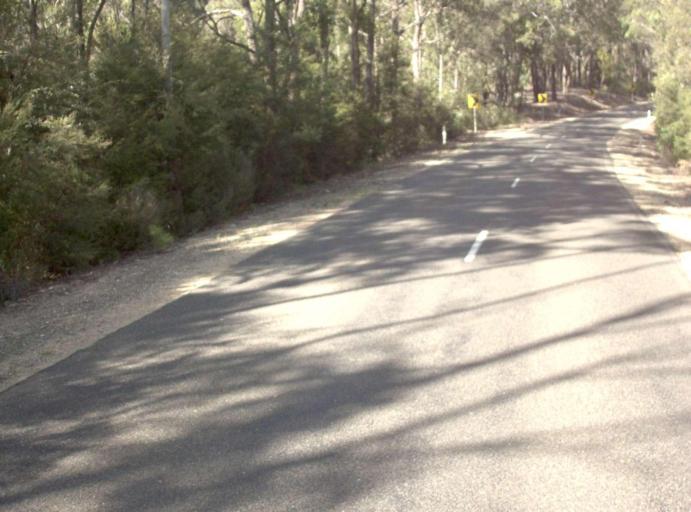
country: AU
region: Victoria
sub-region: East Gippsland
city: Lakes Entrance
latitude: -37.6597
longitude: 148.0866
